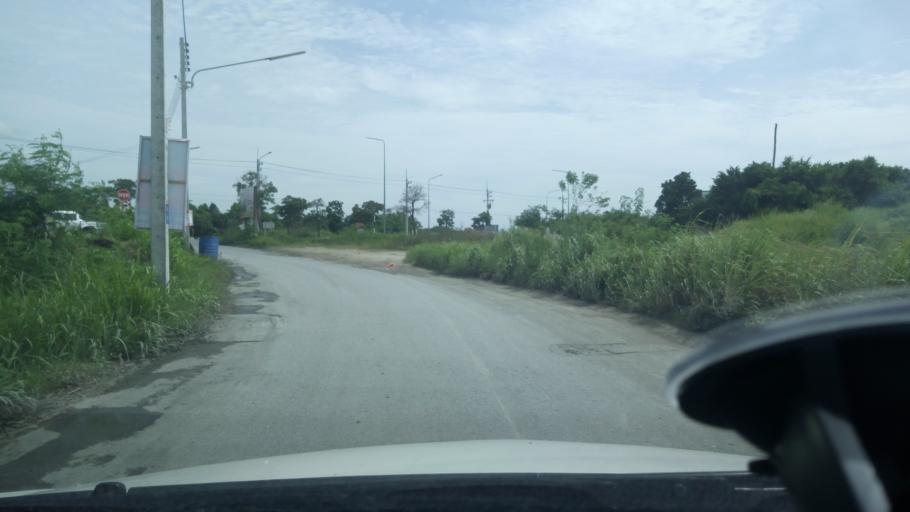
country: TH
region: Chon Buri
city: Chon Buri
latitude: 13.2877
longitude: 100.9661
